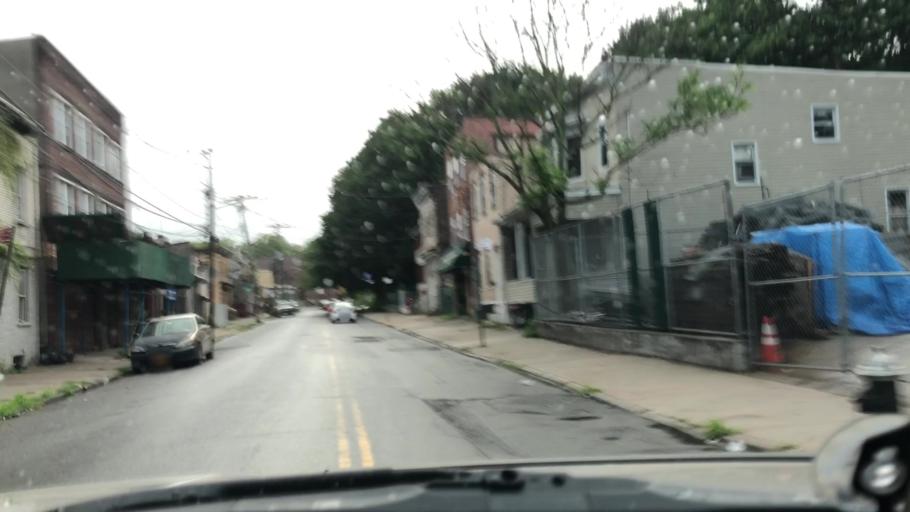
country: US
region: New Jersey
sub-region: Hudson County
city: Bayonne
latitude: 40.6375
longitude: -74.0883
